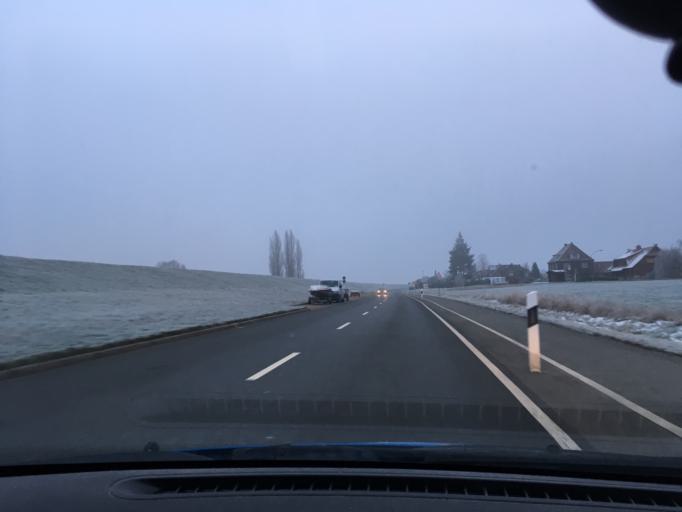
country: DE
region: Lower Saxony
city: Stelle
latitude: 53.4402
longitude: 10.0914
